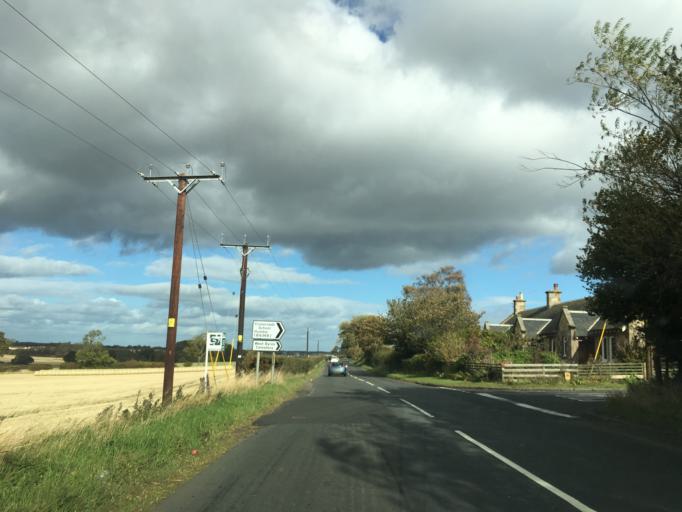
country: GB
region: Scotland
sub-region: East Lothian
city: Ormiston
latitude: 55.8973
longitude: -2.9521
